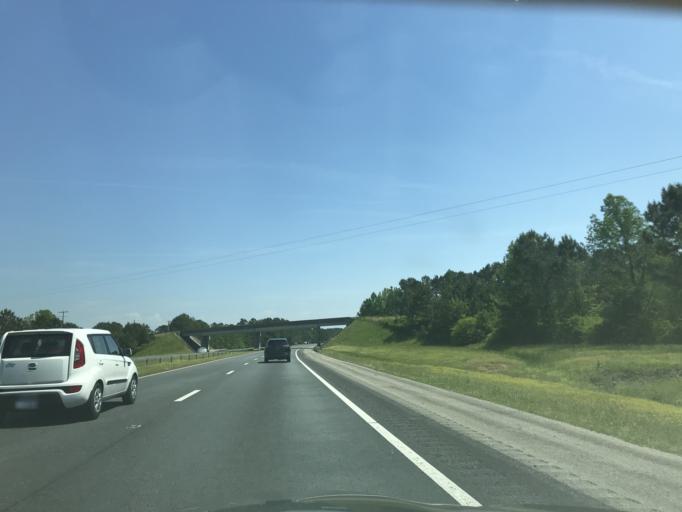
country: US
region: North Carolina
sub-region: Johnston County
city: Benson
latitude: 35.3683
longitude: -78.4952
